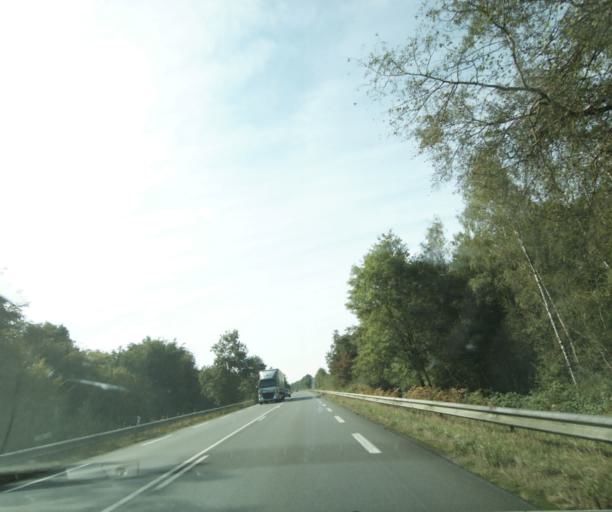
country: FR
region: Bourgogne
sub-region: Departement de Saone-et-Loire
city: Palinges
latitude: 46.5345
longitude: 4.1690
